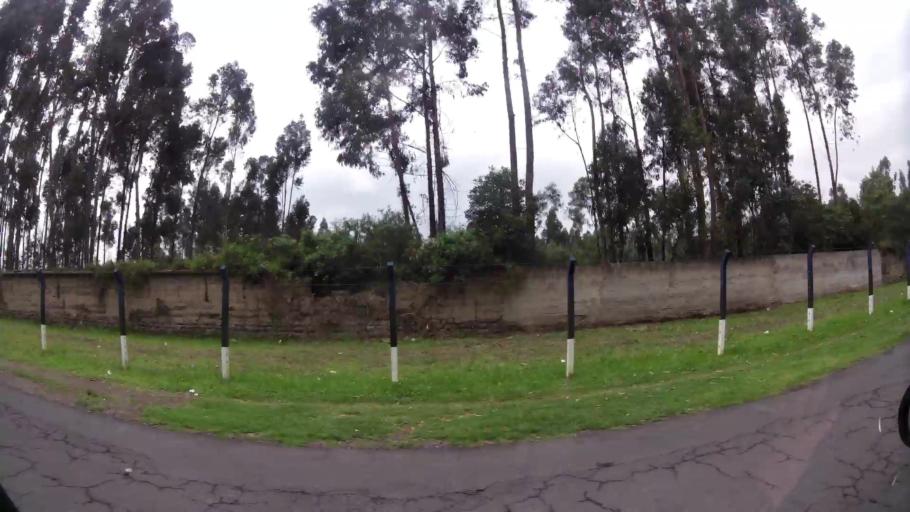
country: EC
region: Pichincha
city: Sangolqui
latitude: -0.3487
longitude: -78.4720
